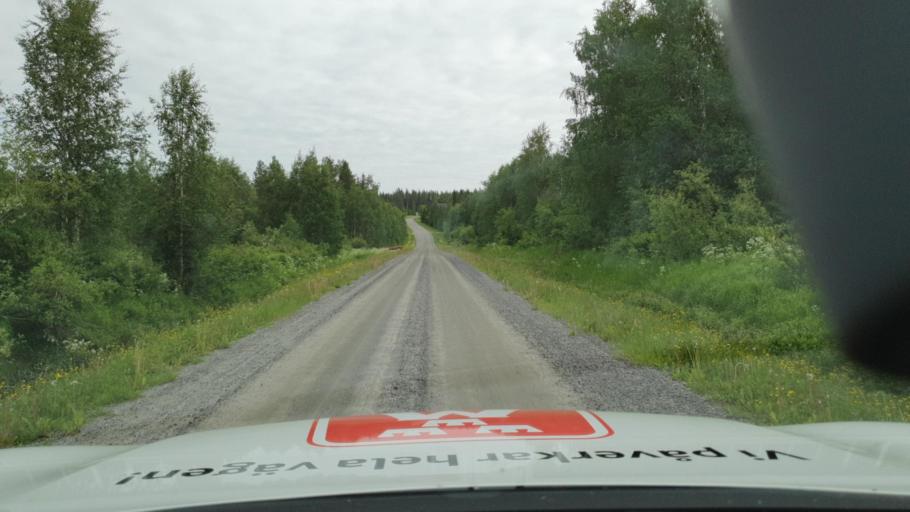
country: SE
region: Vaesterbotten
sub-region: Skelleftea Kommun
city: Langsele
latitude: 64.4788
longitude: 20.2342
